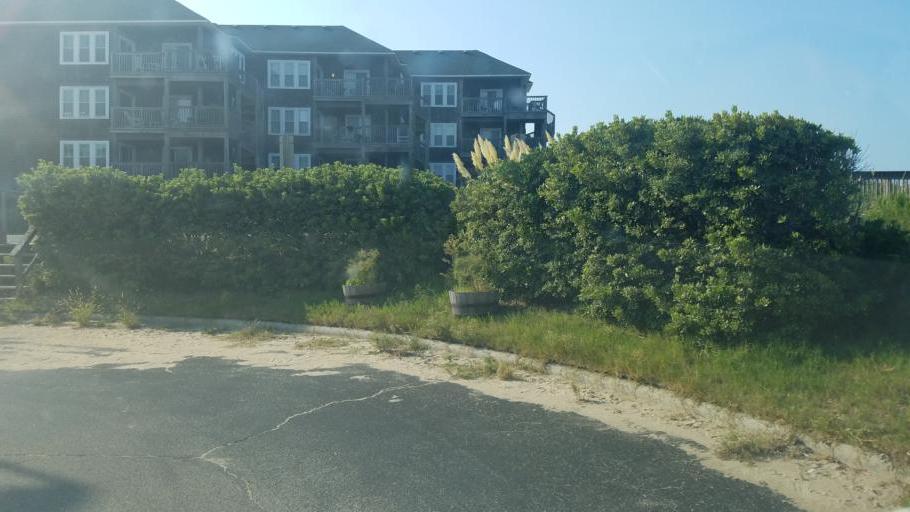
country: US
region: North Carolina
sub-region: Dare County
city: Kill Devil Hills
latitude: 36.0176
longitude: -75.6579
